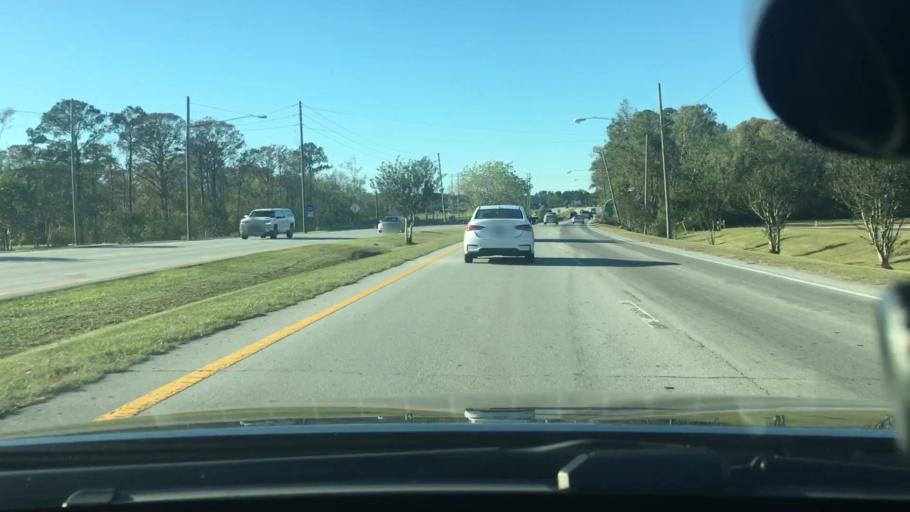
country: US
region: North Carolina
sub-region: Craven County
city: Havelock
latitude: 34.8899
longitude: -76.9211
